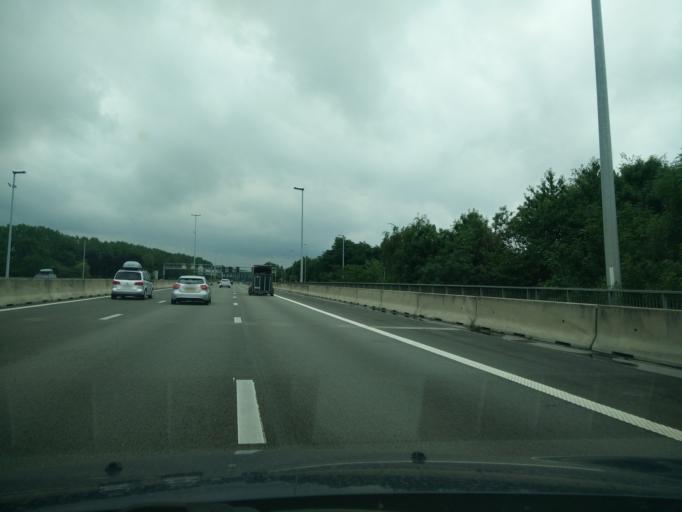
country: BE
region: Flanders
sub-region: Provincie Oost-Vlaanderen
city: Merelbeke
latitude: 51.0106
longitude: 3.7261
